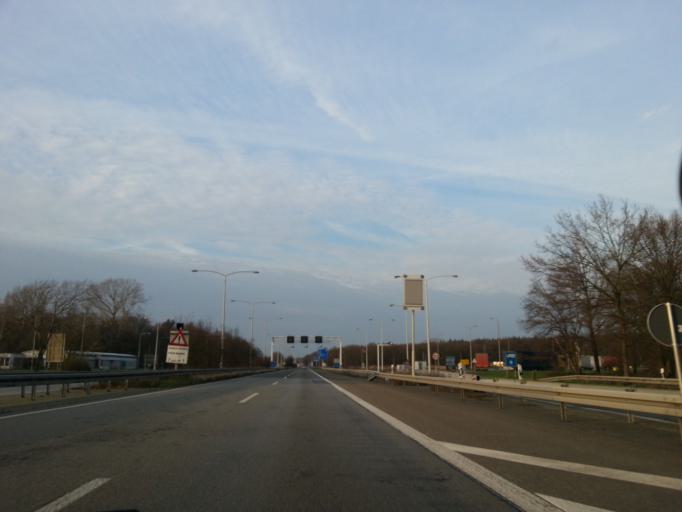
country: NL
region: Gelderland
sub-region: Gemeente Montferland
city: s-Heerenberg
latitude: 51.8983
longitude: 6.1661
